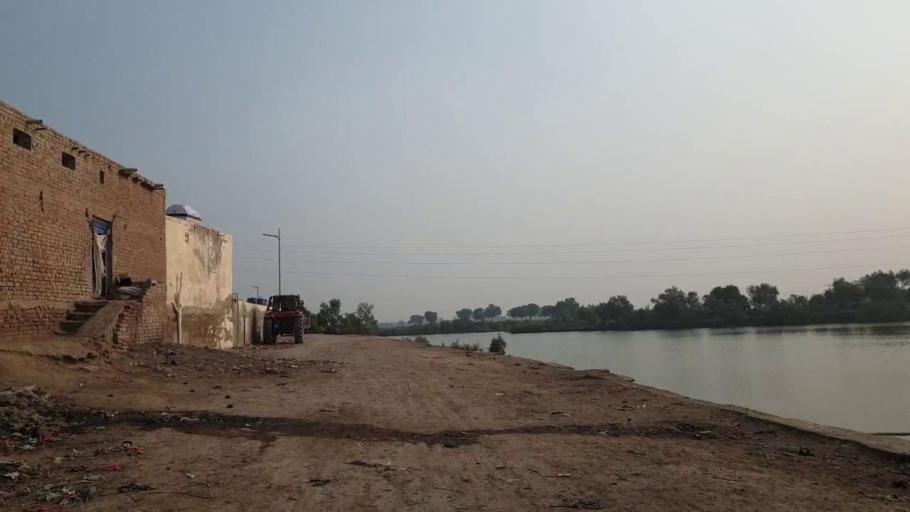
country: PK
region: Sindh
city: Bhan
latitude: 26.4721
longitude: 67.7062
